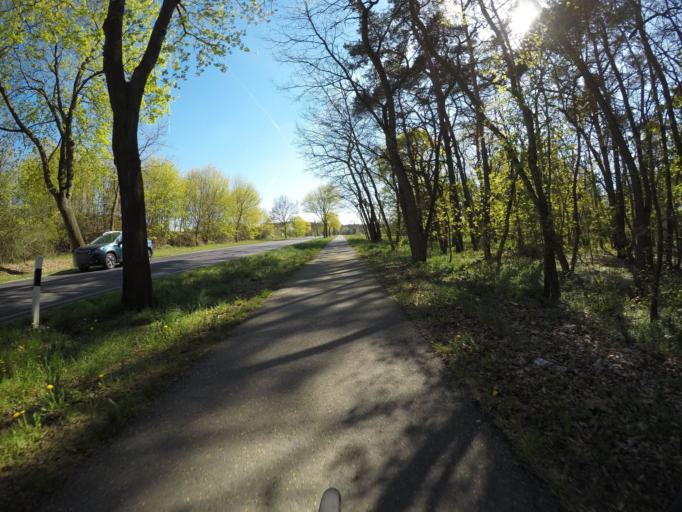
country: DE
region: Brandenburg
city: Rehfelde
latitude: 52.4928
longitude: 13.9178
